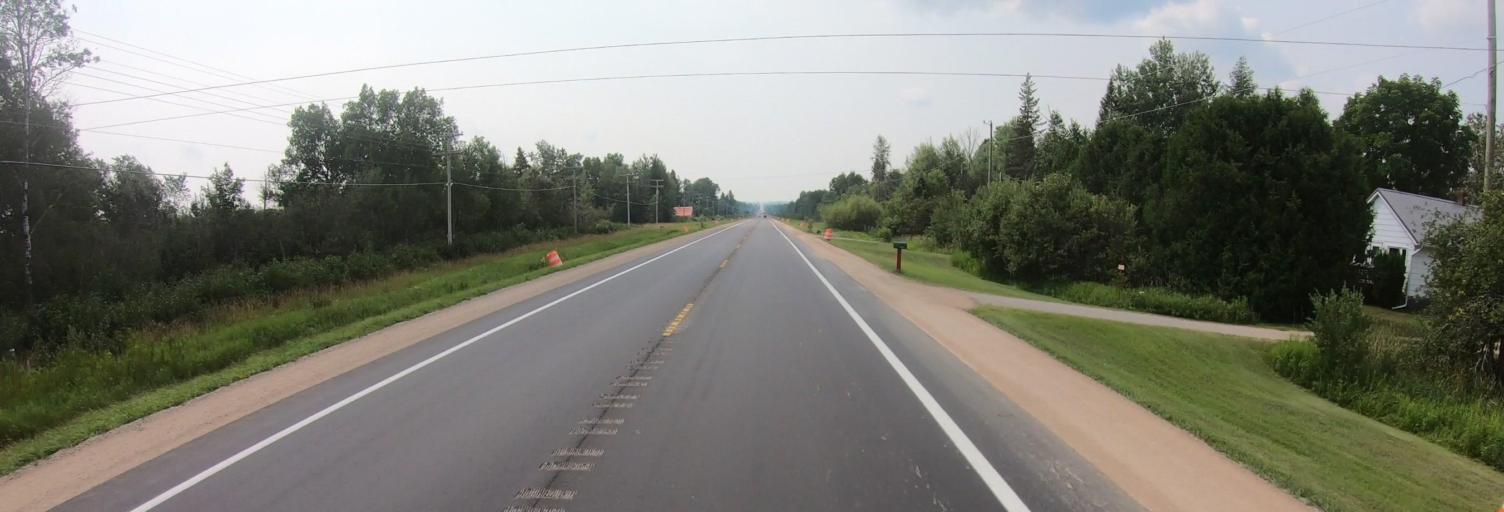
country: US
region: Michigan
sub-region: Luce County
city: Newberry
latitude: 46.3882
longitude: -85.5099
